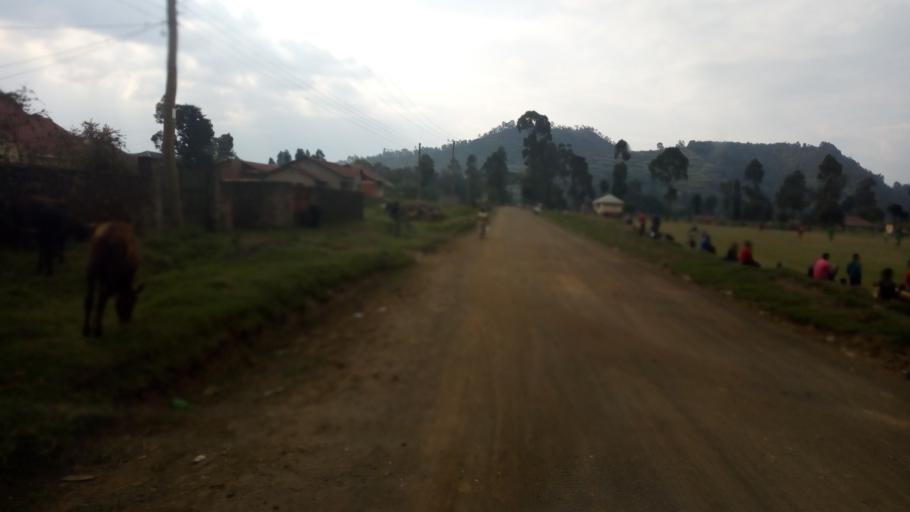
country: UG
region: Western Region
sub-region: Kisoro District
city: Kisoro
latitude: -1.2876
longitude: 29.6906
